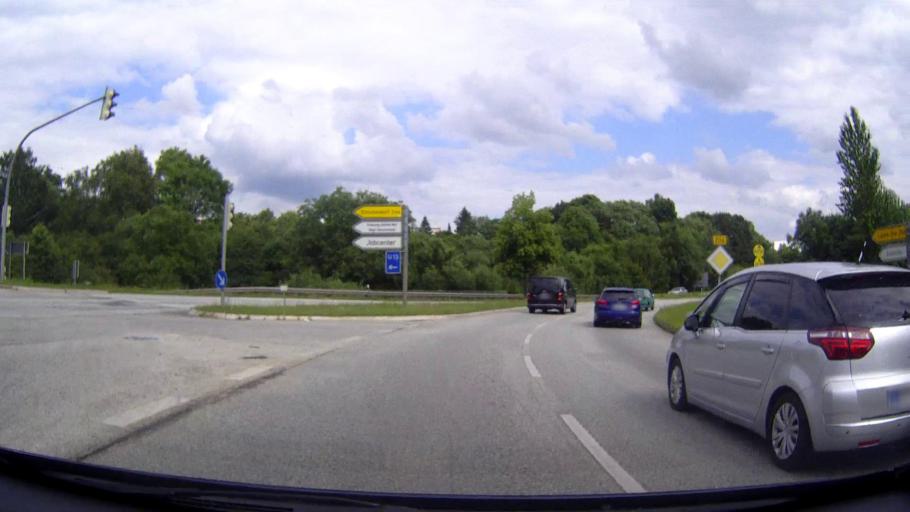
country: DE
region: Schleswig-Holstein
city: Bad Segeberg
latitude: 53.9382
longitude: 10.2917
